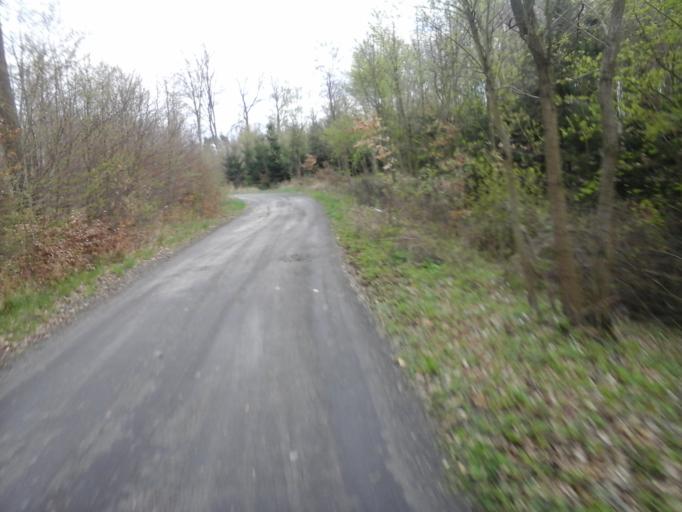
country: PL
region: West Pomeranian Voivodeship
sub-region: Powiat choszczenski
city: Bierzwnik
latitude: 53.0666
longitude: 15.5861
